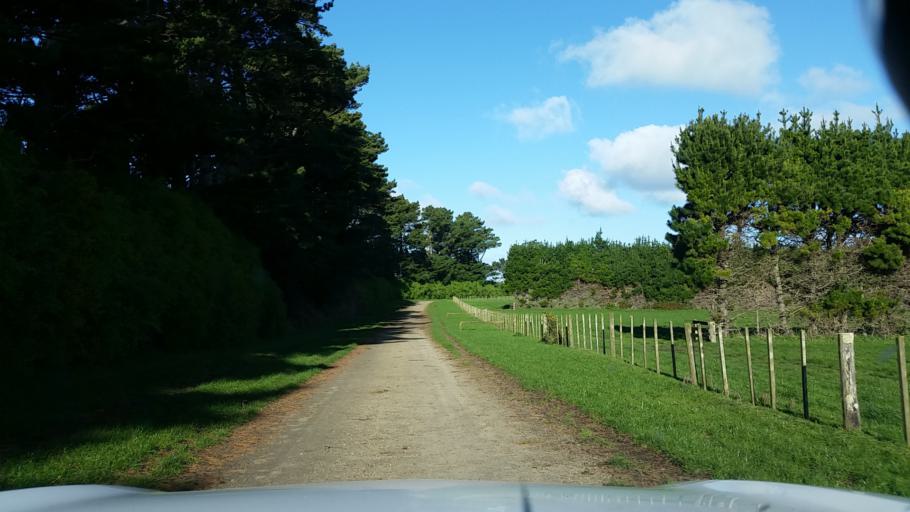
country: NZ
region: Taranaki
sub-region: South Taranaki District
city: Patea
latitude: -39.7390
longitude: 174.5423
